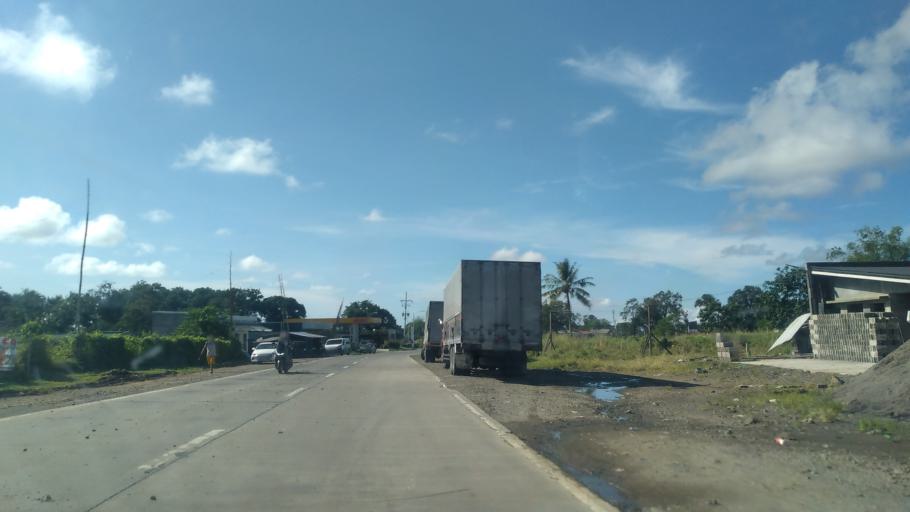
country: PH
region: Calabarzon
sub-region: Province of Quezon
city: Isabang
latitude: 13.9541
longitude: 121.5789
